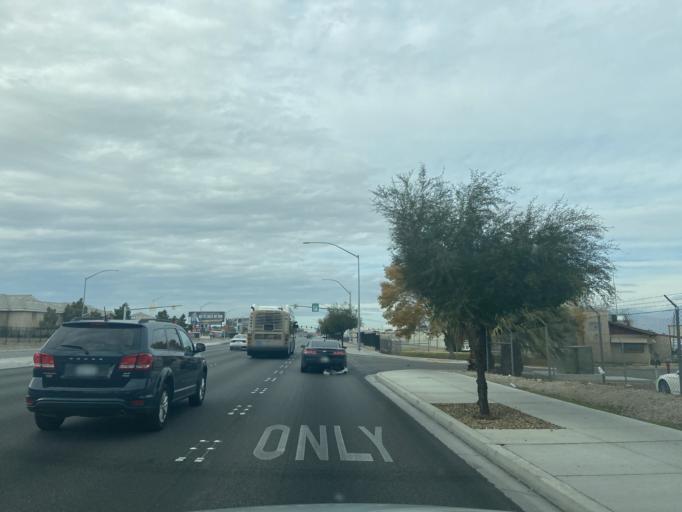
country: US
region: Nevada
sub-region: Clark County
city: Las Vegas
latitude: 36.2108
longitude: -115.2061
